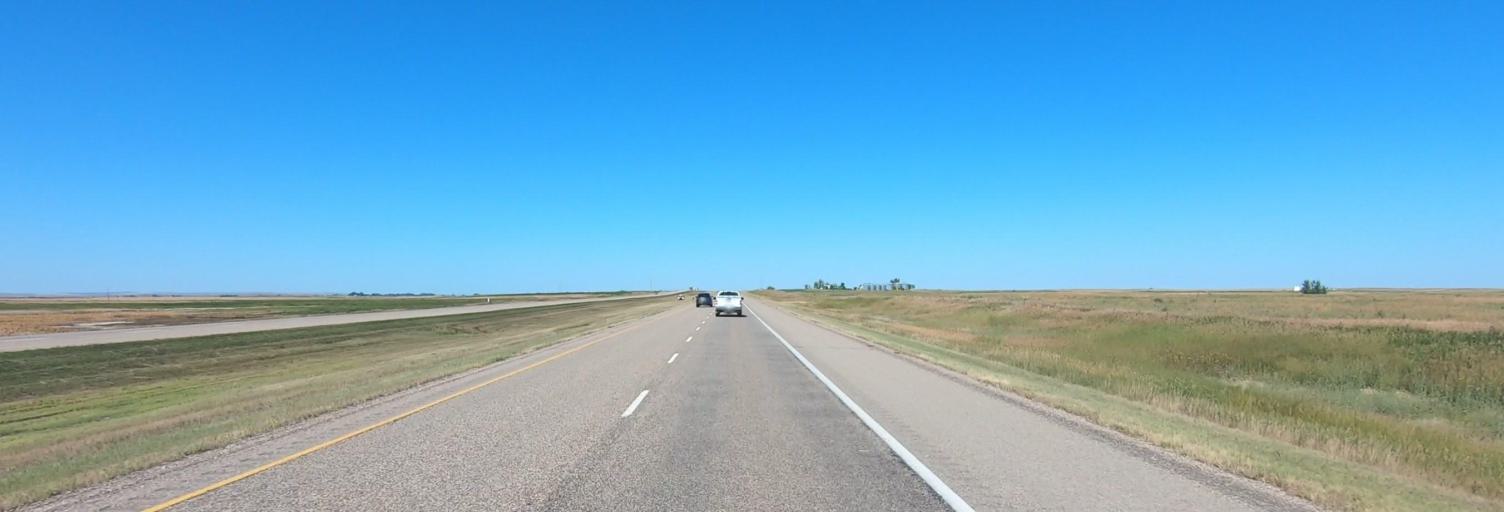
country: CA
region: Alberta
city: Bassano
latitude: 50.7141
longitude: -112.2573
